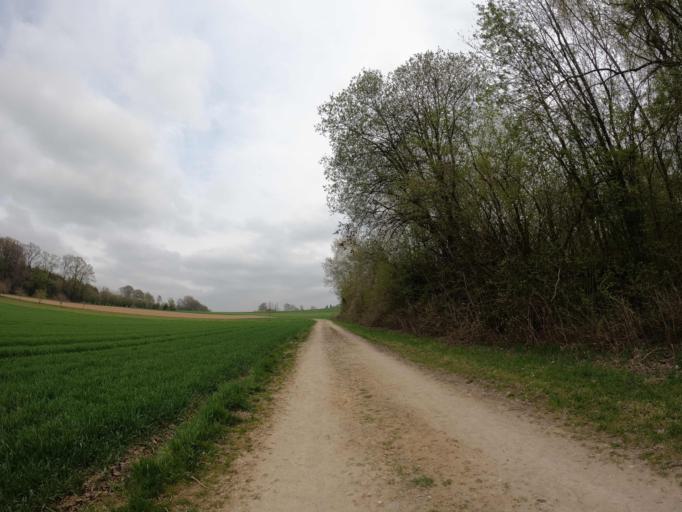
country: DE
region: Bavaria
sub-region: Upper Bavaria
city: Anzing
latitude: 48.1378
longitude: 11.8357
